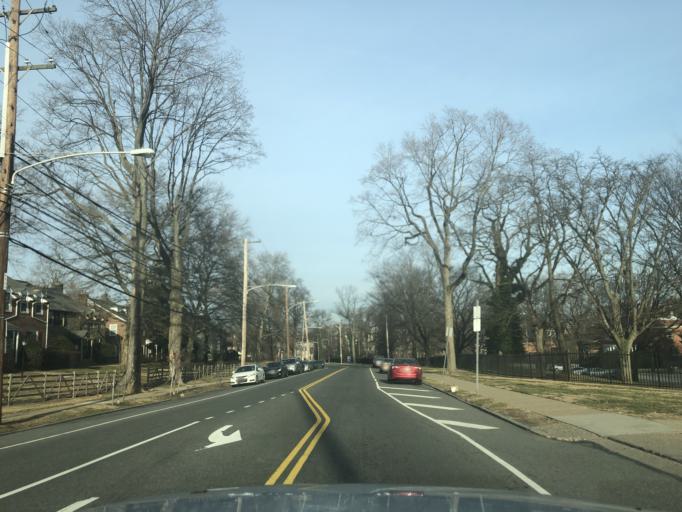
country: US
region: Pennsylvania
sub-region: Montgomery County
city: Bala-Cynwyd
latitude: 40.0199
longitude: -75.1812
